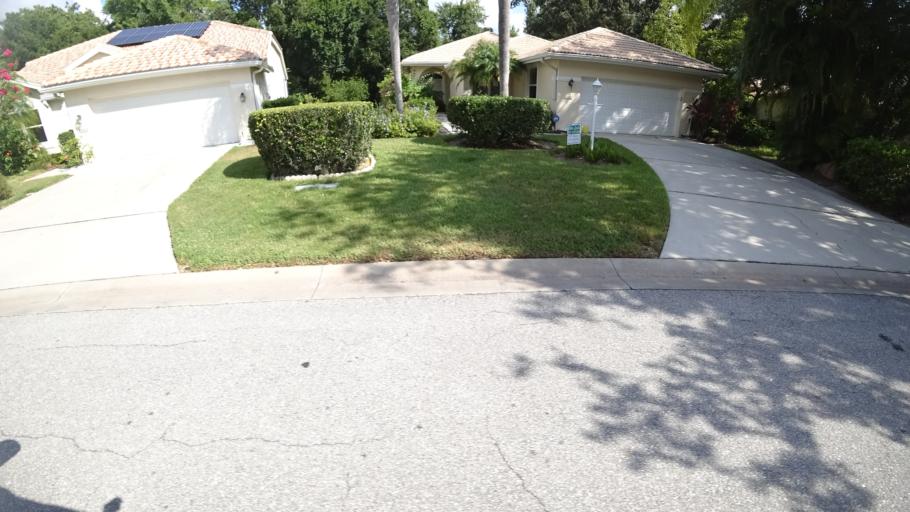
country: US
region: Florida
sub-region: Sarasota County
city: The Meadows
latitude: 27.4232
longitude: -82.4367
